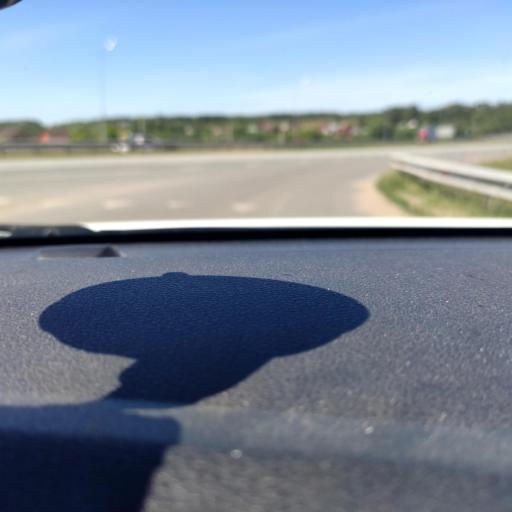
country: RU
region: Tatarstan
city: Vysokaya Gora
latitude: 55.7531
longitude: 49.3844
